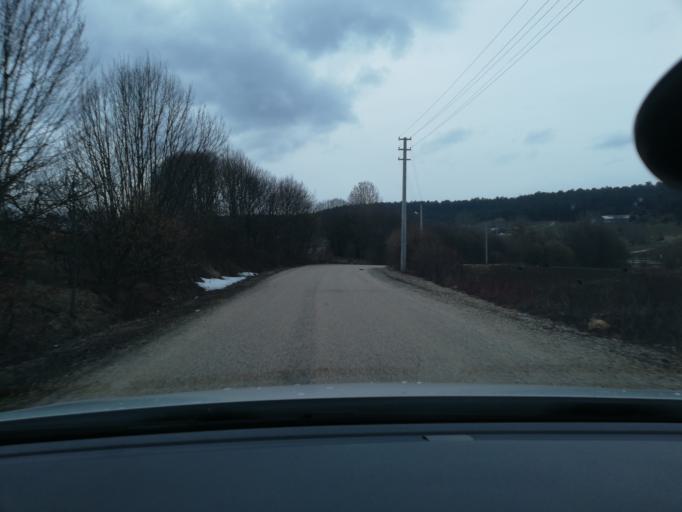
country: TR
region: Bolu
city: Yenicaga
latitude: 40.7562
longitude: 31.9303
